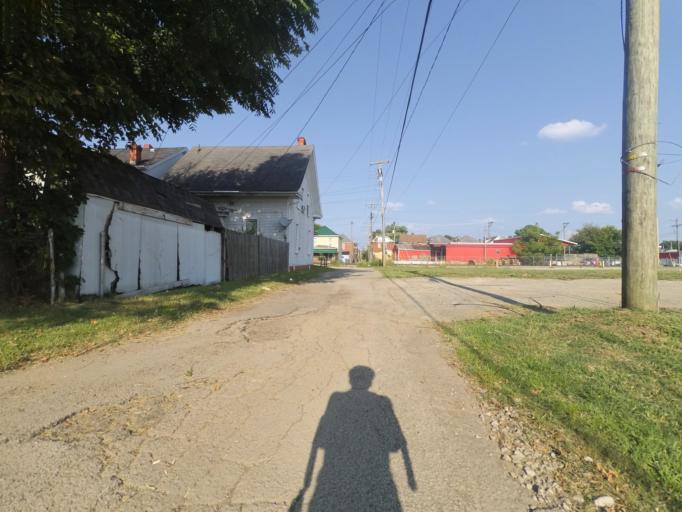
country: US
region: West Virginia
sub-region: Cabell County
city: Huntington
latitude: 38.4155
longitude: -82.4537
